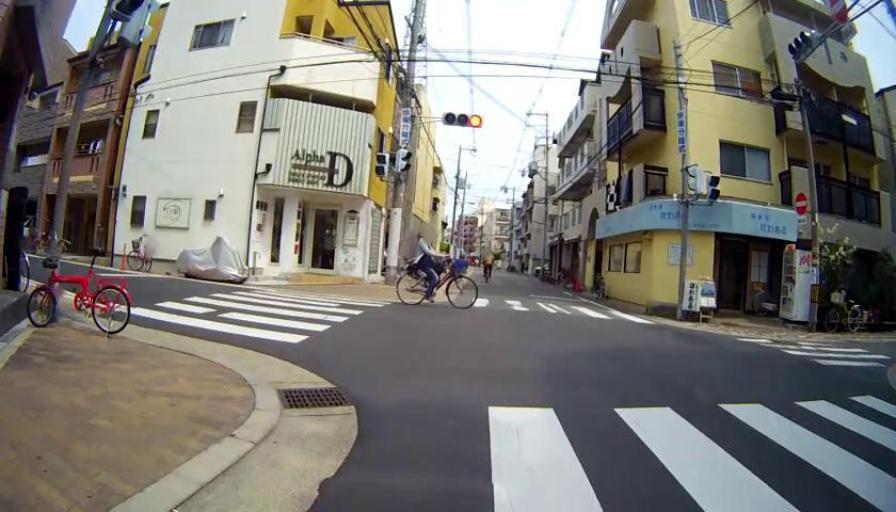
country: JP
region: Osaka
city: Suita
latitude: 34.7463
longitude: 135.5373
